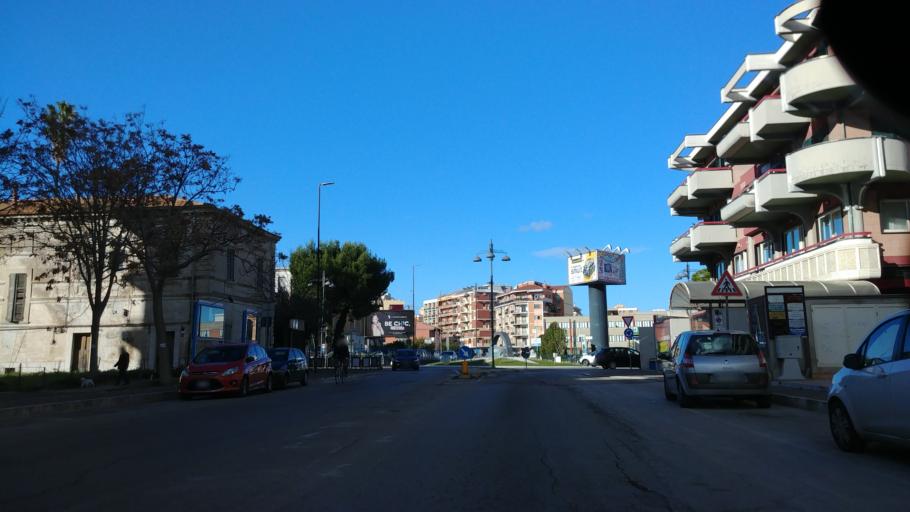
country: IT
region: Molise
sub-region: Provincia di Campobasso
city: Termoli
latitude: 41.9975
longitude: 14.9946
